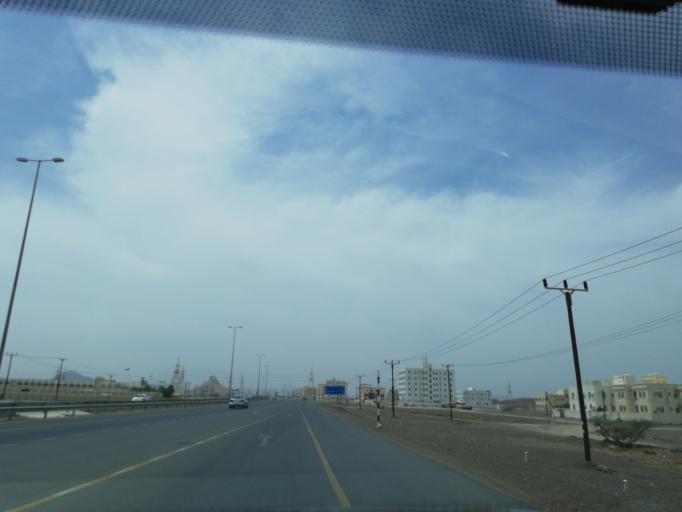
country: OM
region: Muhafazat ad Dakhiliyah
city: Nizwa
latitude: 22.8592
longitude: 57.5177
